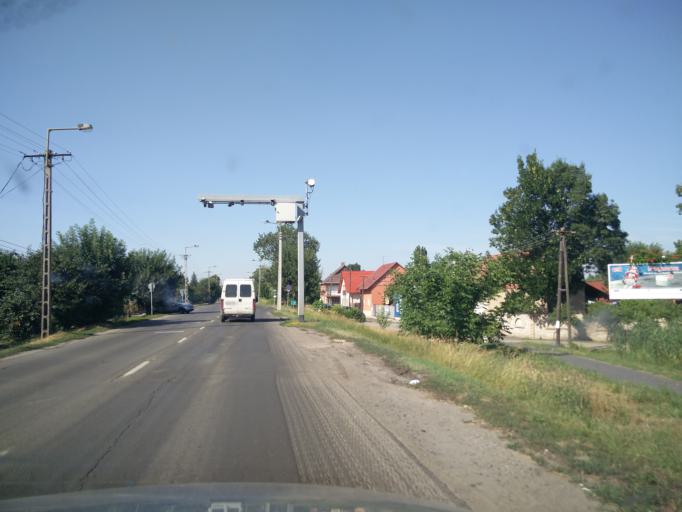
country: HU
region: Csongrad
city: Szeged
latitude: 46.2775
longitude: 20.1669
